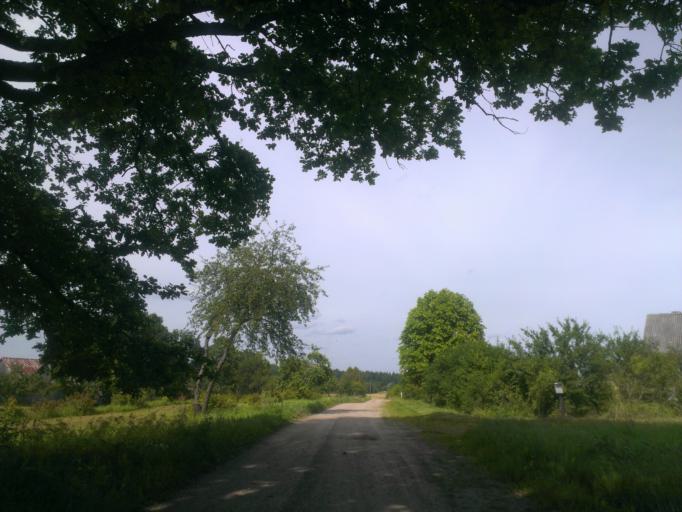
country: LV
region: Ligatne
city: Ligatne
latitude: 57.2234
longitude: 25.0073
